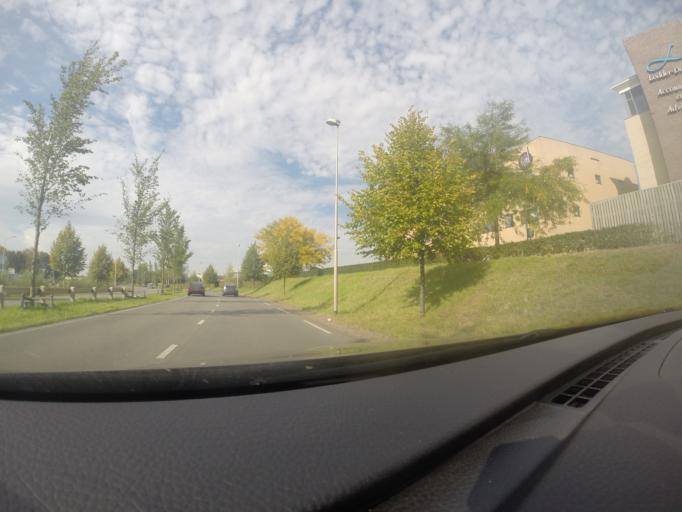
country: NL
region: Gelderland
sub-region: Gemeente Doetinchem
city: Doetinchem
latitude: 51.9518
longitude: 6.3029
